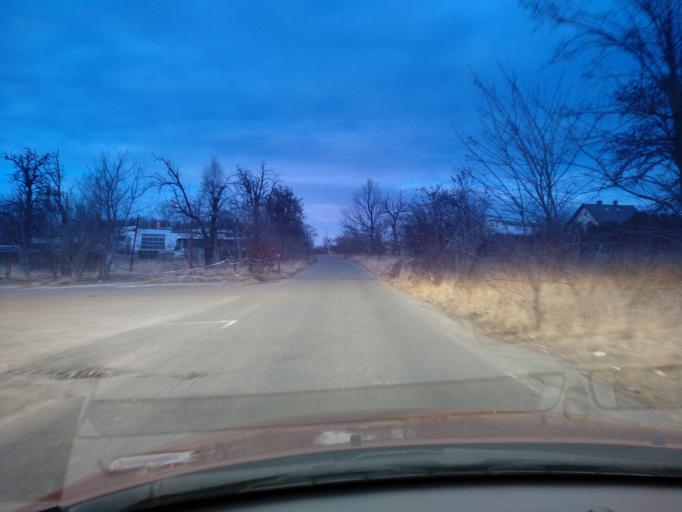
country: PL
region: Lower Silesian Voivodeship
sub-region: Powiat zgorzelecki
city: Zgorzelec
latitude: 51.1507
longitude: 15.0194
